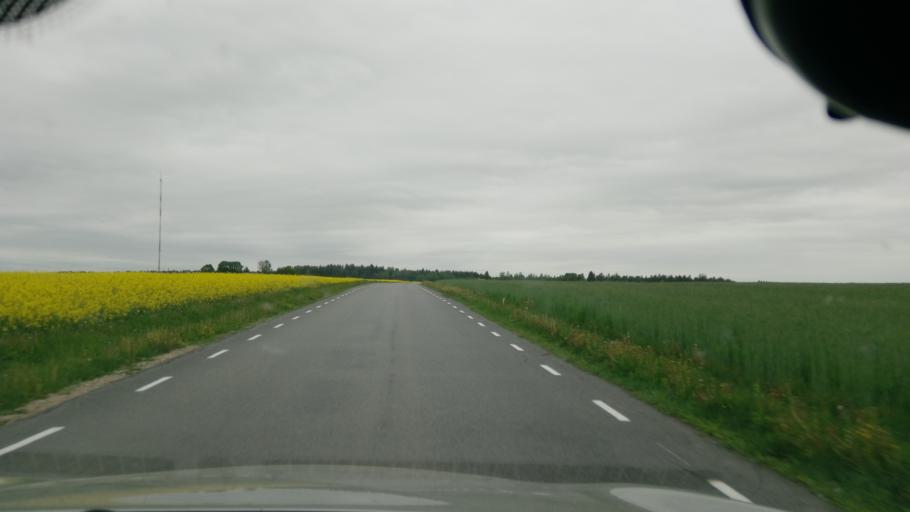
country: EE
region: Jaervamaa
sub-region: Koeru vald
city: Koeru
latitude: 58.9964
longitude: 26.0640
